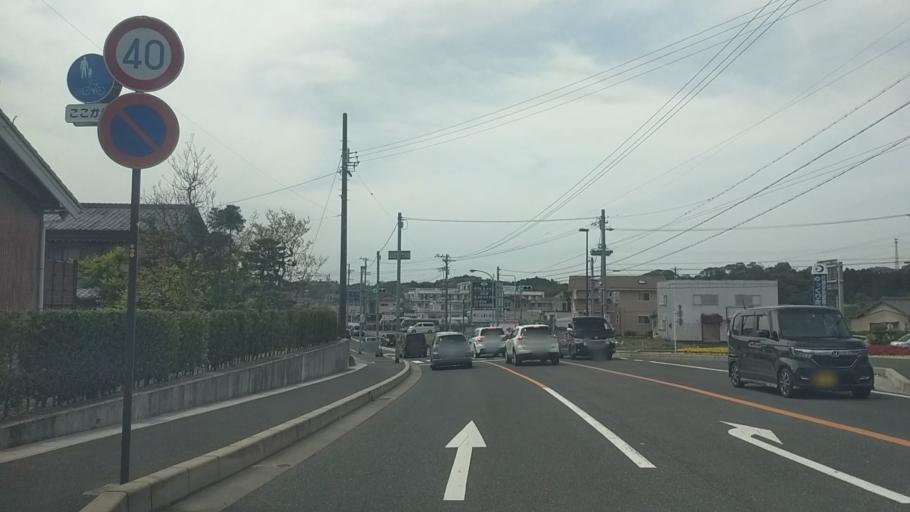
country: JP
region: Shizuoka
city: Kosai-shi
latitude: 34.7580
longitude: 137.5118
